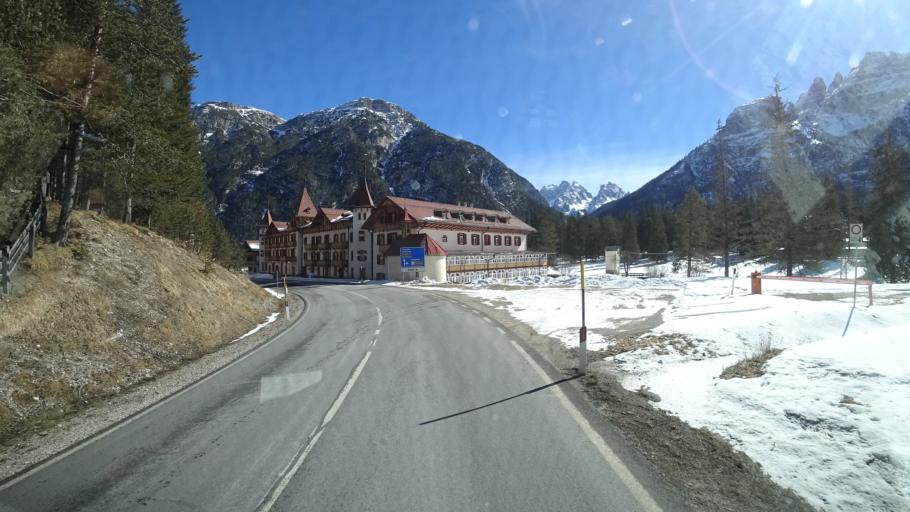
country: IT
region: Trentino-Alto Adige
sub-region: Bolzano
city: Dobbiaco
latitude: 46.6203
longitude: 12.2155
